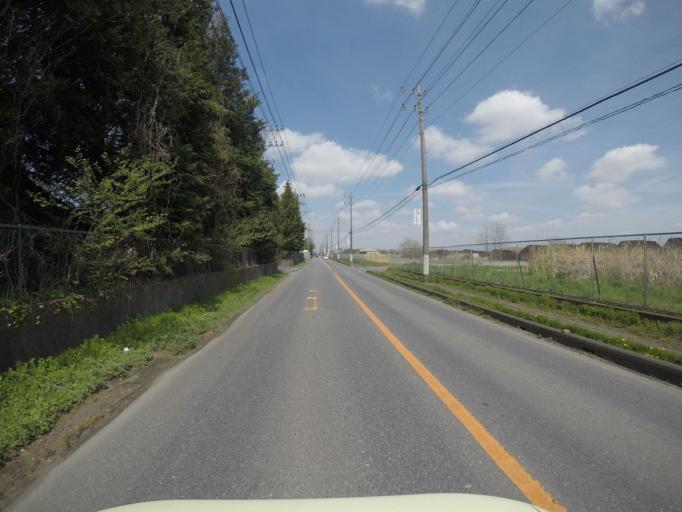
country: JP
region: Ibaraki
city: Tsukuba
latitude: 36.2318
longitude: 140.0572
